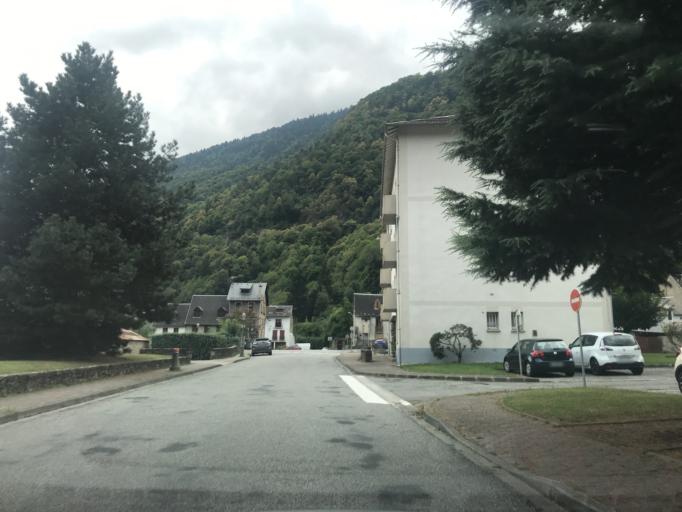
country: FR
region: Midi-Pyrenees
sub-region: Departement de la Haute-Garonne
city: Bagneres-de-Luchon
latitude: 42.7929
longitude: 0.5875
